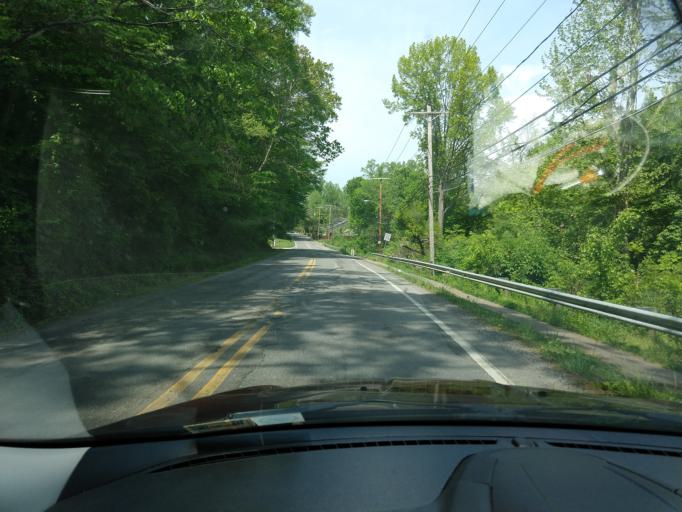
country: US
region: West Virginia
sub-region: Kanawha County
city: Saint Albans
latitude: 38.3758
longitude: -81.7969
